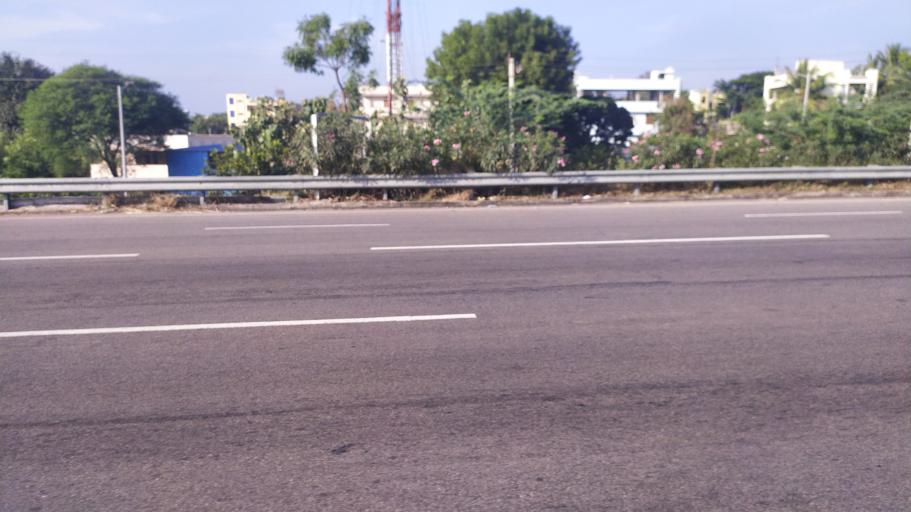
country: IN
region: Telangana
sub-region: Hyderabad
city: Hyderabad
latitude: 17.3410
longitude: 78.3649
